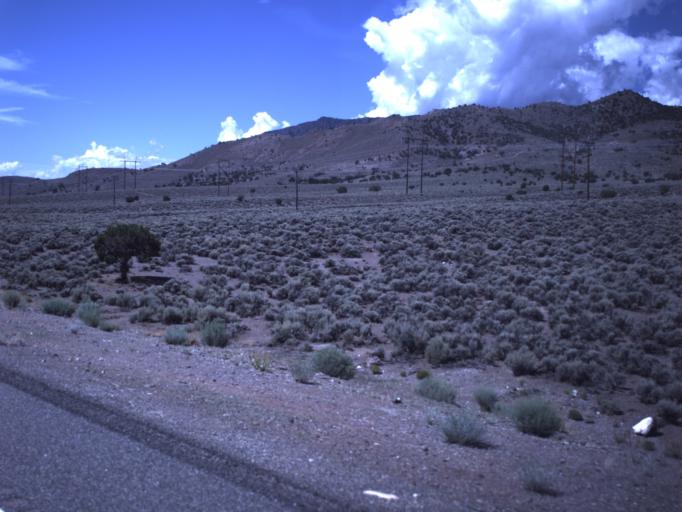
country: US
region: Utah
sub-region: Piute County
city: Junction
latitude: 38.3168
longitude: -112.2209
